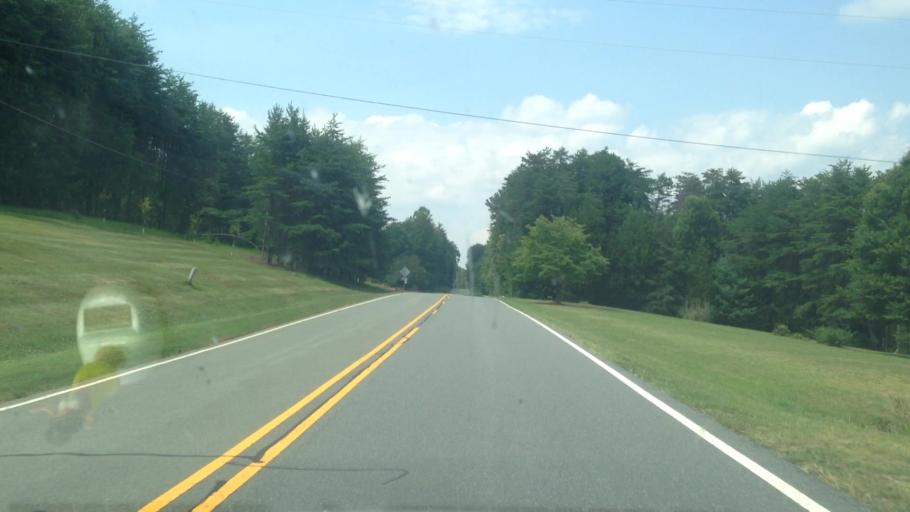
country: US
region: North Carolina
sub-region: Stokes County
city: Walnut Cove
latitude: 36.3891
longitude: -80.0952
